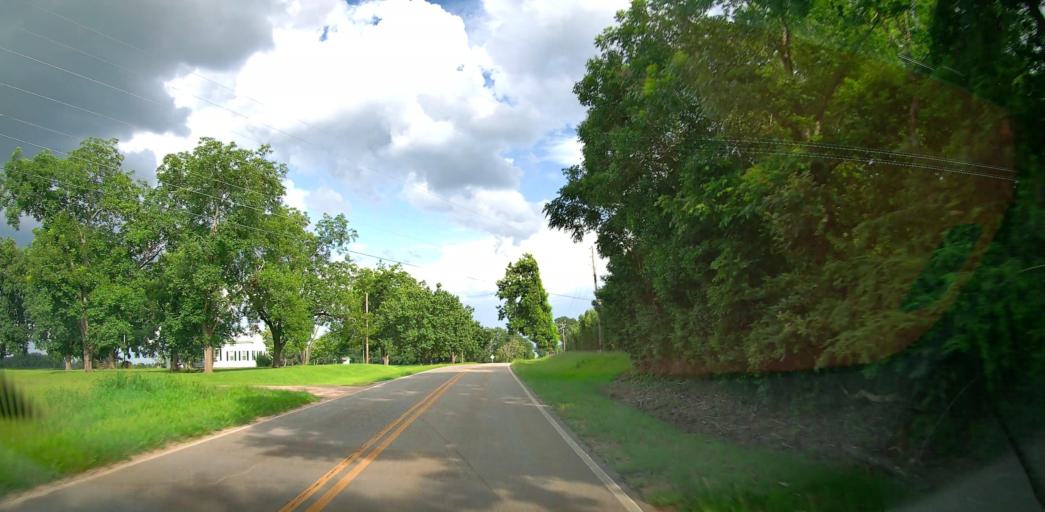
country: US
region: Georgia
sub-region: Bleckley County
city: Cochran
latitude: 32.4057
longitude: -83.3814
